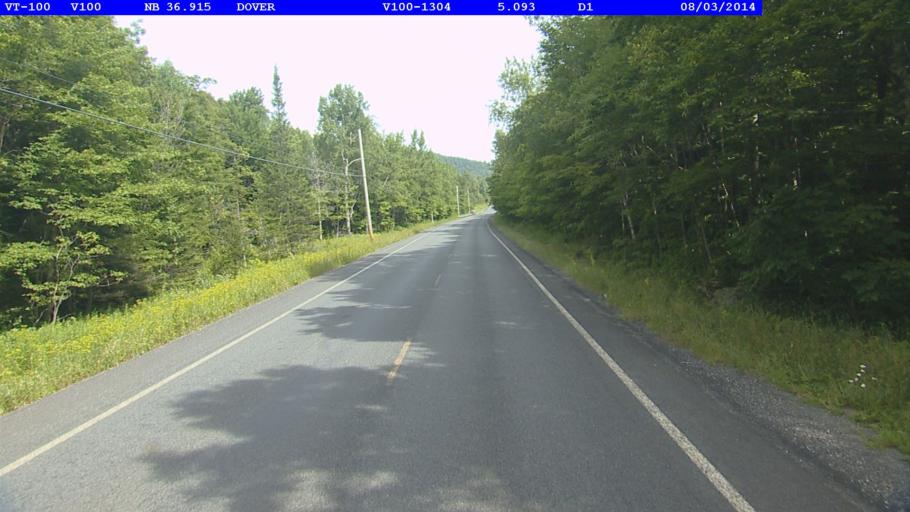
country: US
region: Vermont
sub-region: Windham County
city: Dover
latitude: 42.9848
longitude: -72.8889
